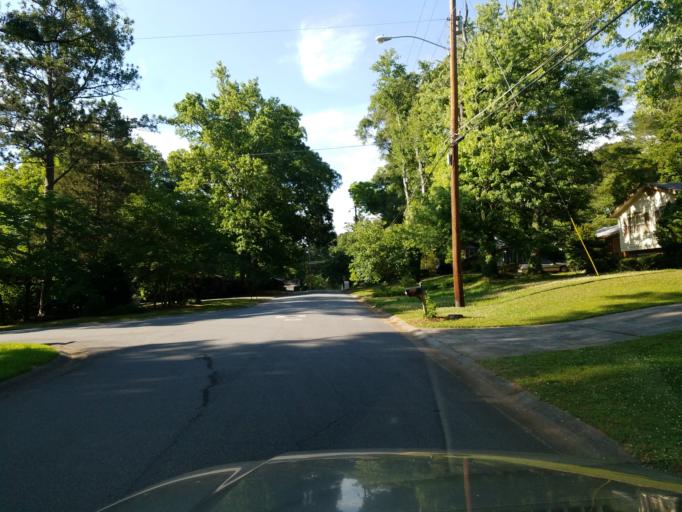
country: US
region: Georgia
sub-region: Cobb County
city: Smyrna
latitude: 33.9320
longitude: -84.4820
